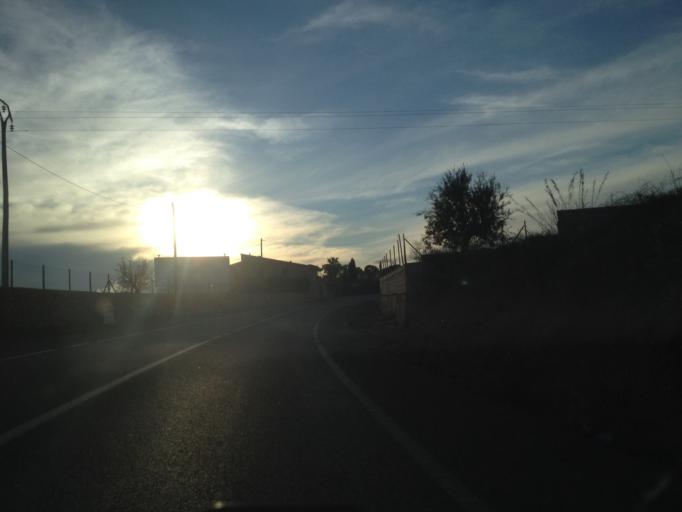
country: ES
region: Balearic Islands
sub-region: Illes Balears
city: Santa Maria del Cami
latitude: 39.6480
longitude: 2.7674
